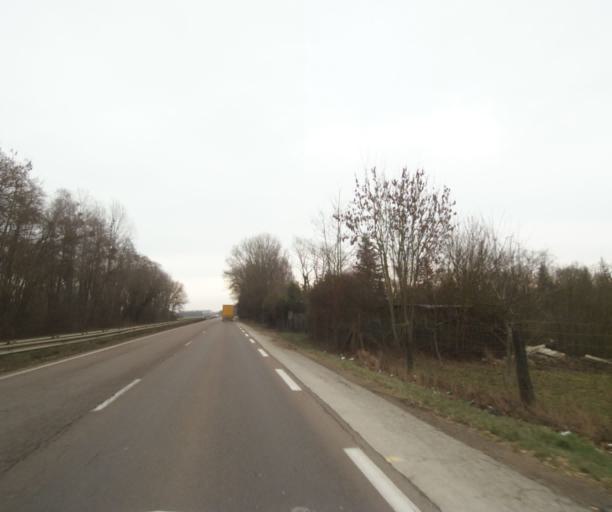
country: FR
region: Champagne-Ardenne
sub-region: Departement de la Haute-Marne
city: Villiers-en-Lieu
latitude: 48.6513
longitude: 4.8438
